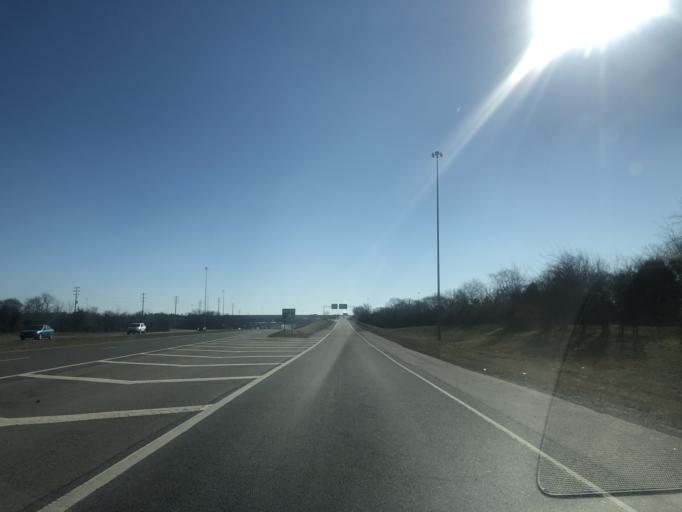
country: US
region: Tennessee
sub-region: Rutherford County
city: Murfreesboro
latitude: 35.9086
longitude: -86.4541
